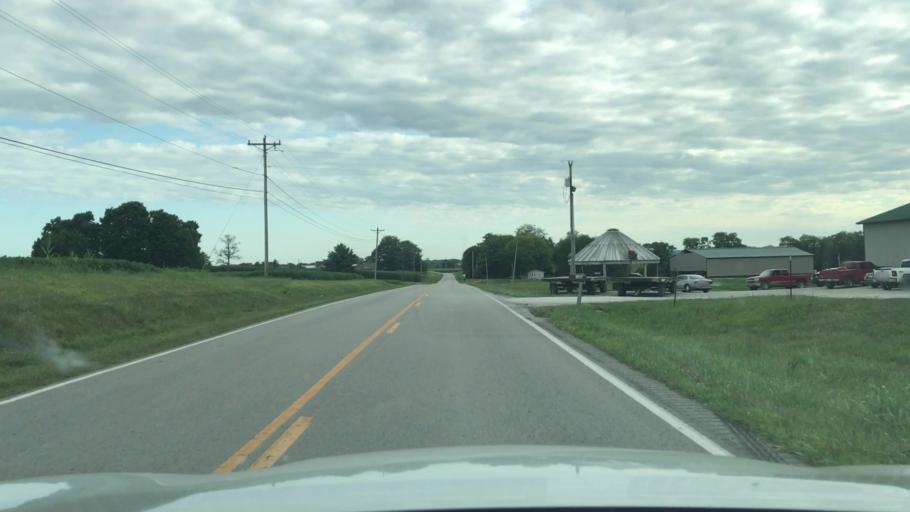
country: US
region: Kentucky
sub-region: Todd County
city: Elkton
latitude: 36.7731
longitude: -87.1661
